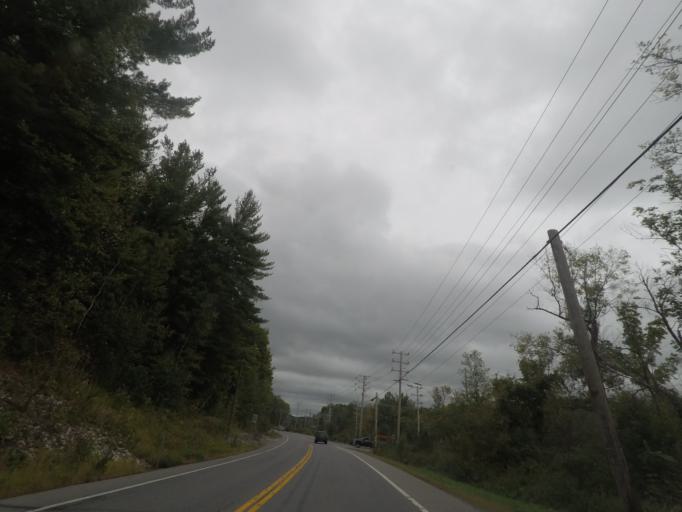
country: US
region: New York
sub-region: Saratoga County
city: Country Knolls
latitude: 42.9223
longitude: -73.7486
